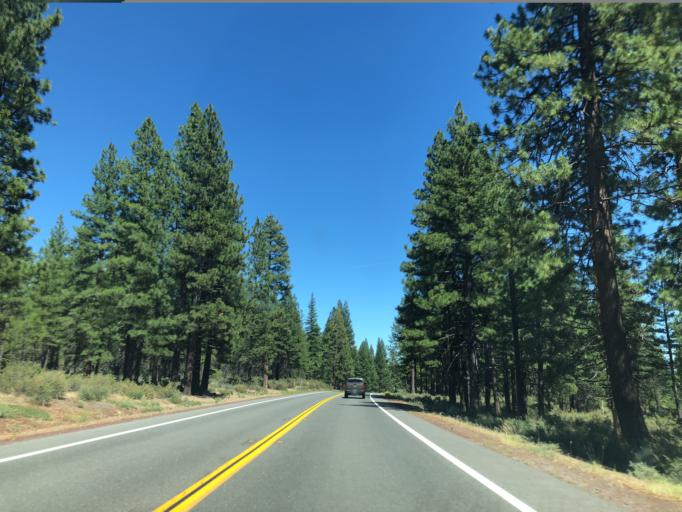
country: US
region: California
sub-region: Lassen County
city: Susanville
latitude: 40.4169
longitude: -120.7731
